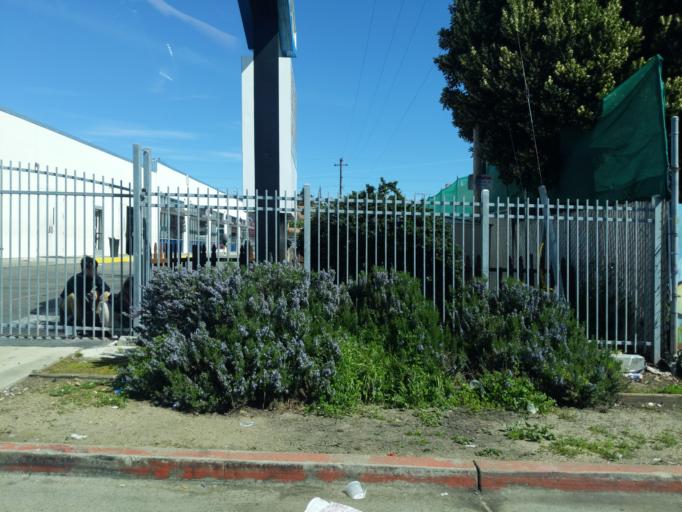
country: US
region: California
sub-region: Alameda County
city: Alameda
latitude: 37.7748
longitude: -122.2132
